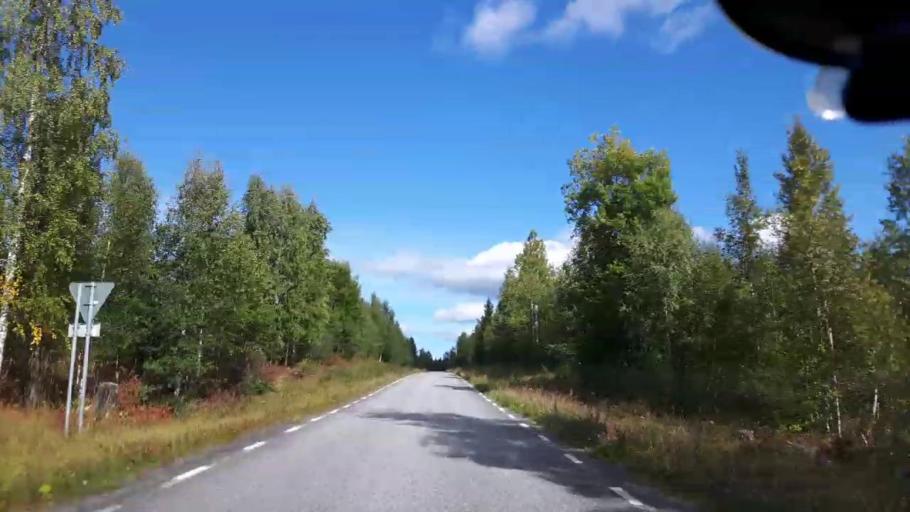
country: SE
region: Jaemtland
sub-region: OEstersunds Kommun
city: Brunflo
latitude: 63.1943
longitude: 15.2202
